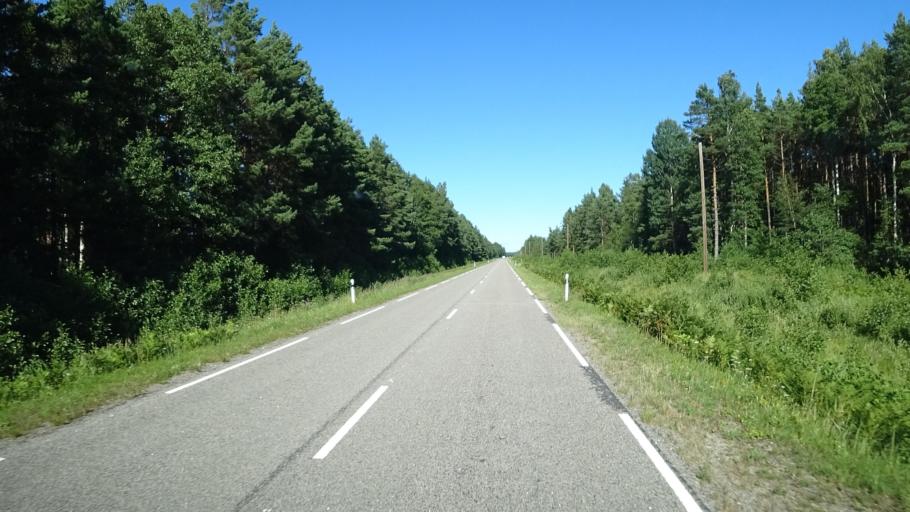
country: LV
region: Dundaga
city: Dundaga
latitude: 57.7060
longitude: 22.4347
